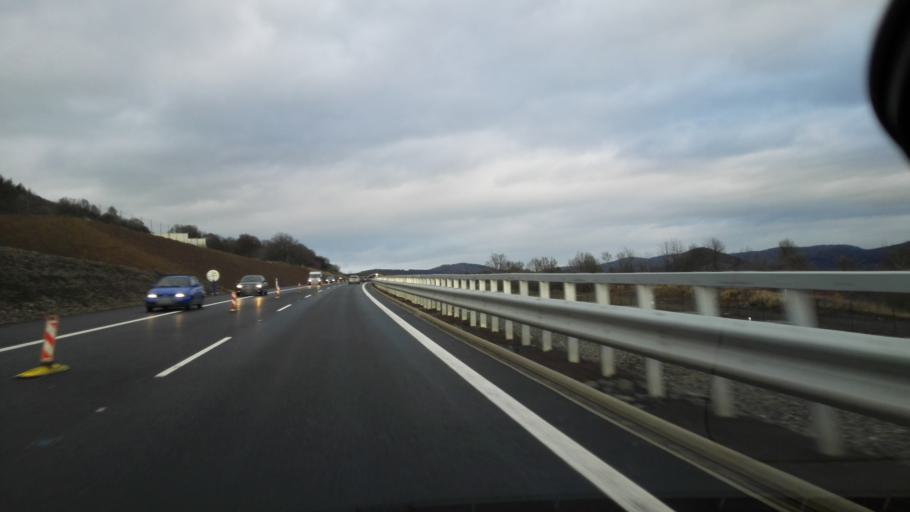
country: CZ
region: Ustecky
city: Velemin
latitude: 50.5608
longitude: 14.0152
